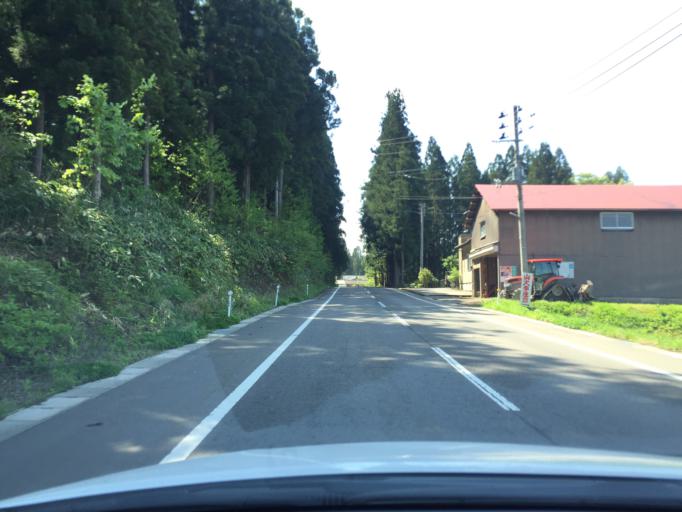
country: JP
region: Niigata
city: Kamo
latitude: 37.5673
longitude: 139.0847
